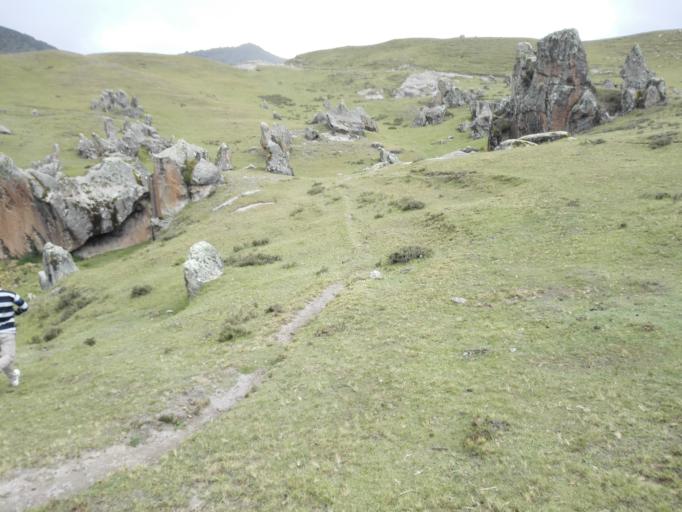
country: PE
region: Ayacucho
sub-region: Provincia de Huamanga
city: Vinchos
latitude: -13.3174
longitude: -74.4508
